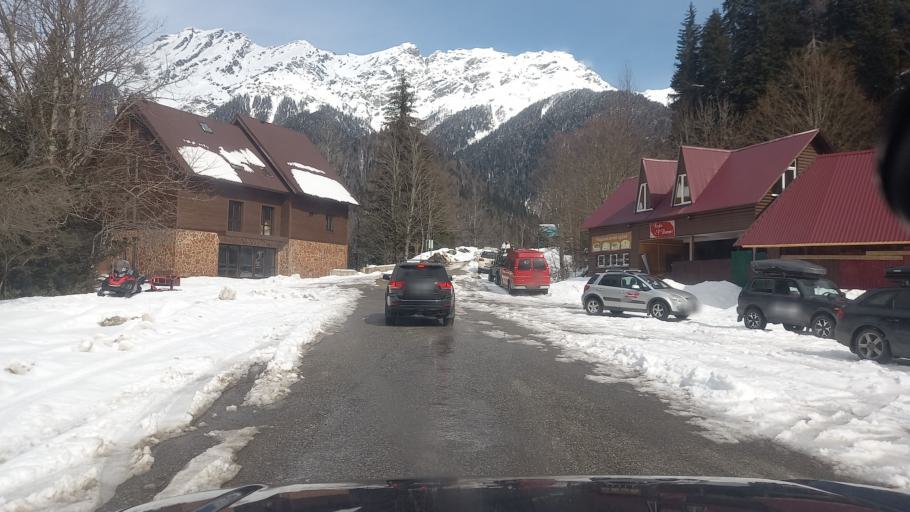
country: GE
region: Abkhazia
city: Gagra
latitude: 43.4752
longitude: 40.5397
